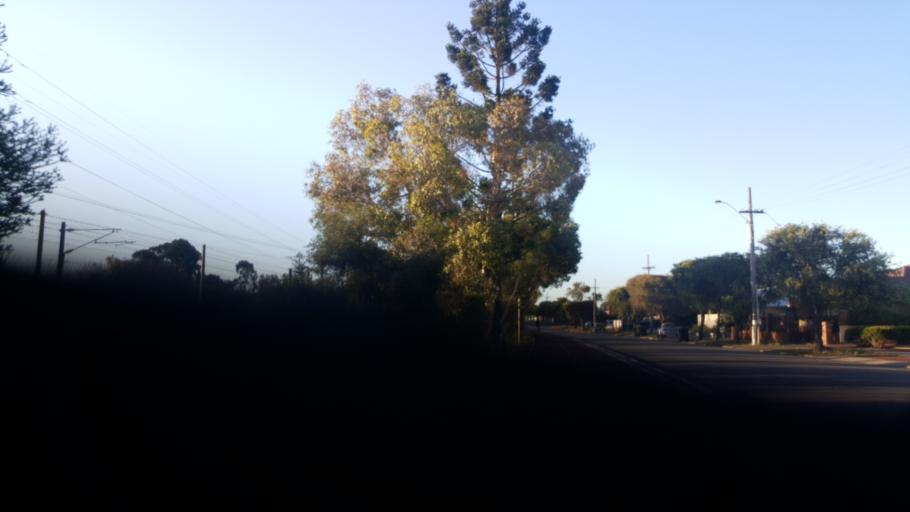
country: AU
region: Western Australia
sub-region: Victoria Park
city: East Victoria Park
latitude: -31.9852
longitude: 115.9151
